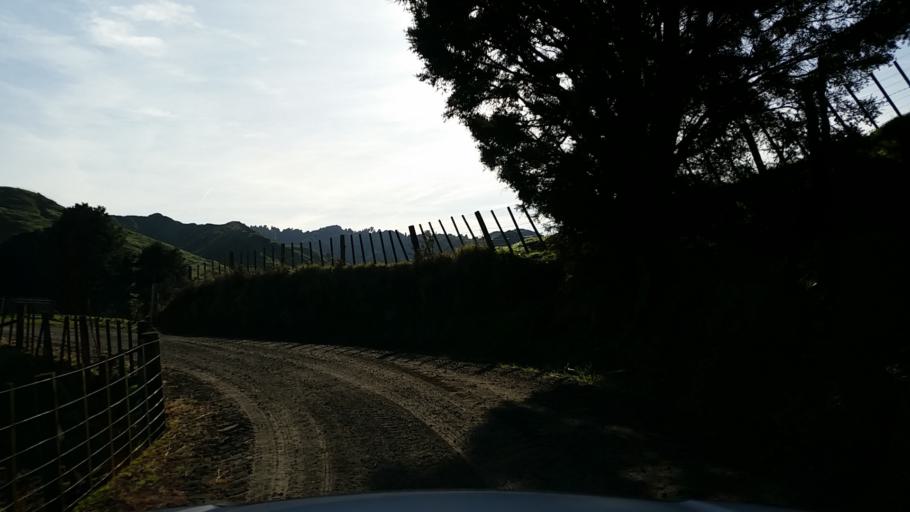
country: NZ
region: Taranaki
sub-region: South Taranaki District
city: Eltham
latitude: -39.3144
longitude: 174.5348
